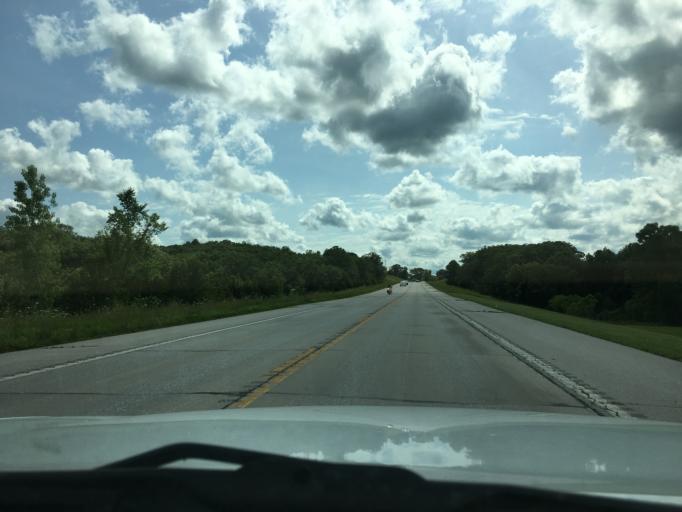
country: US
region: Missouri
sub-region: Franklin County
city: Gerald
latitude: 38.4136
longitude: -91.3057
